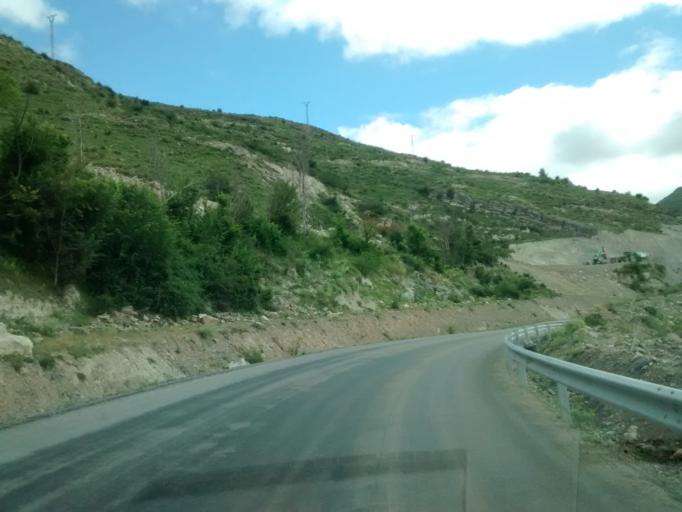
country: ES
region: La Rioja
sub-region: Provincia de La Rioja
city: Terroba
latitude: 42.2594
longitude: -2.4407
